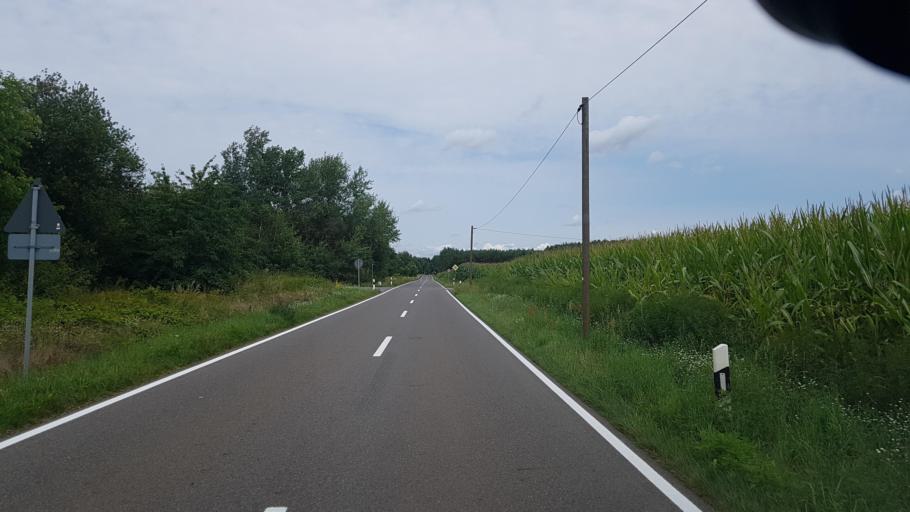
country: DE
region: Brandenburg
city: Spremberg
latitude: 51.6127
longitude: 14.3423
